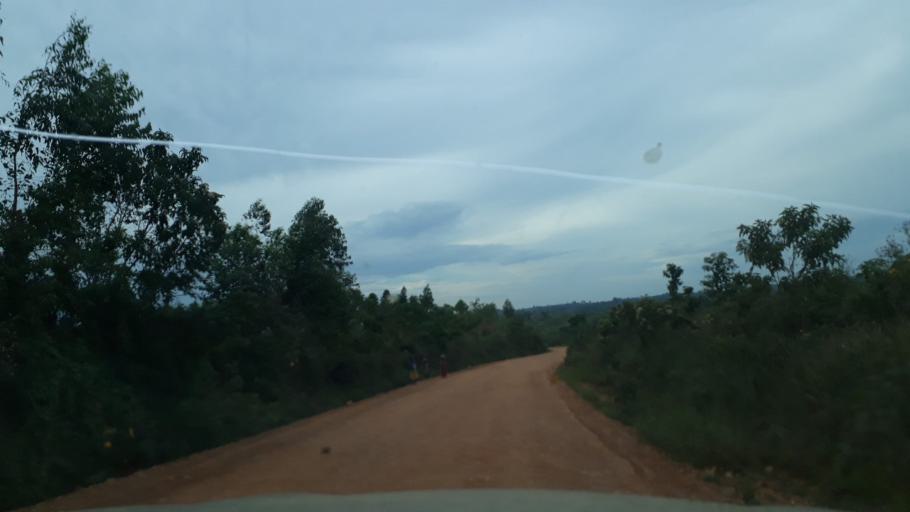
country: UG
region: Northern Region
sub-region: Zombo District
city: Paidha
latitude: 2.0628
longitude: 30.6279
